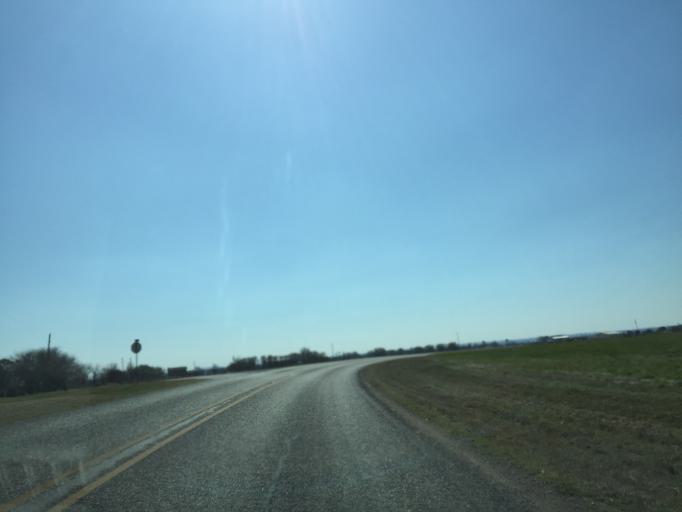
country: US
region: Texas
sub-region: Williamson County
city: Serenada
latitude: 30.6903
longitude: -97.5853
